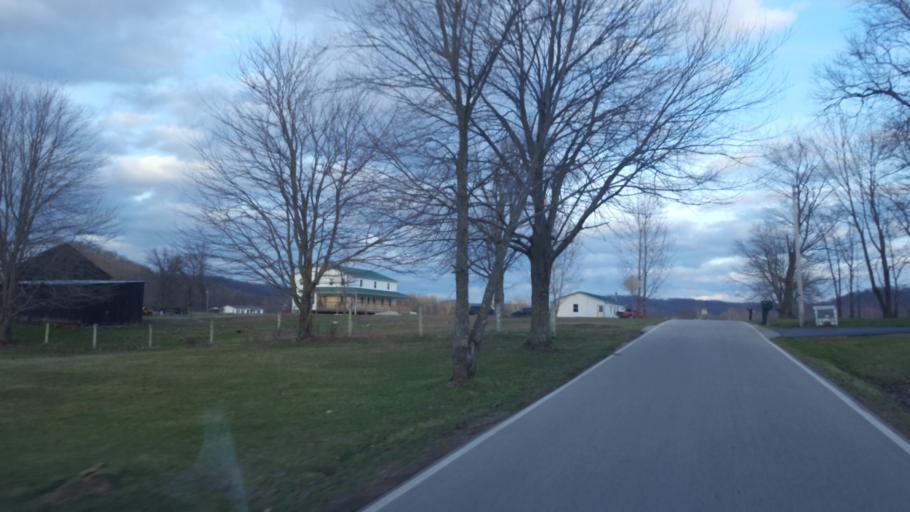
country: US
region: Kentucky
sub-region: Fleming County
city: Flemingsburg
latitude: 38.4957
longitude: -83.5726
